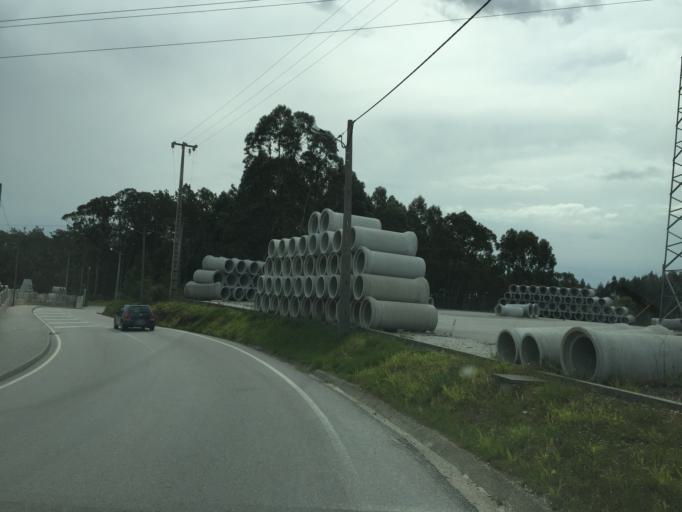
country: PT
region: Leiria
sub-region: Leiria
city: Caranguejeira
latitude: 39.8317
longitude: -8.7295
